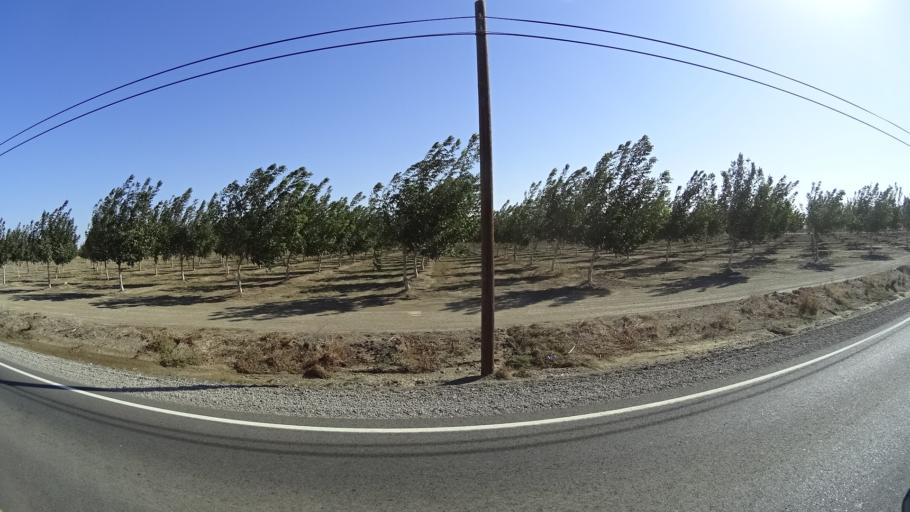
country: US
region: California
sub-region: Yolo County
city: Cottonwood
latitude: 38.6234
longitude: -121.9715
